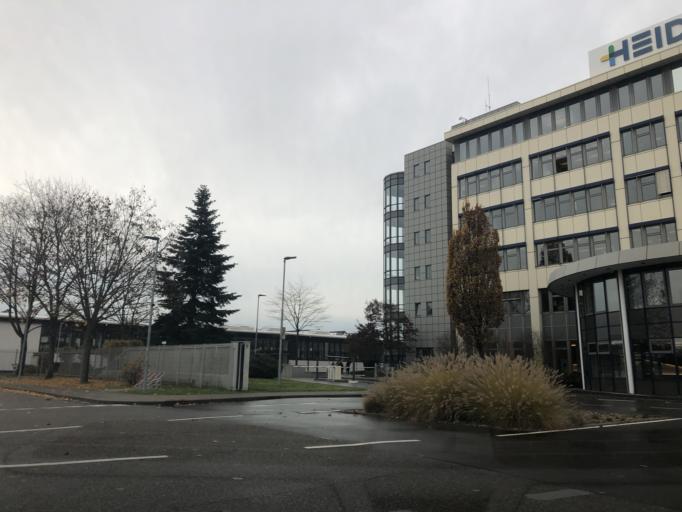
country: DE
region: Baden-Wuerttemberg
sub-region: Karlsruhe Region
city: Walldorf
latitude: 49.2891
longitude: 8.6552
